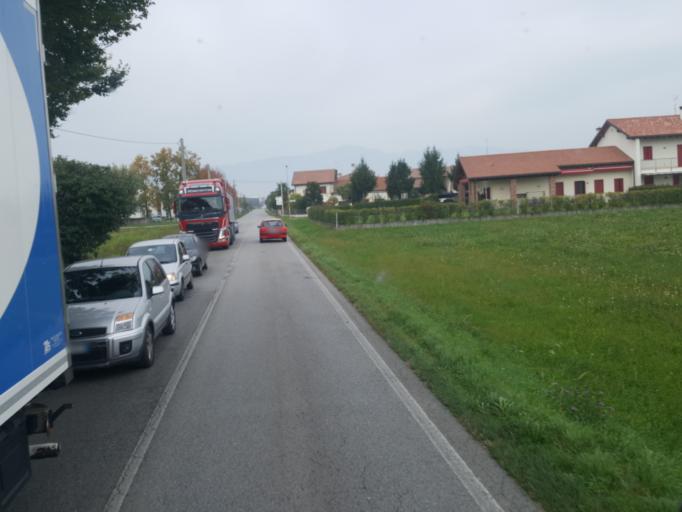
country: IT
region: Veneto
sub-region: Provincia di Treviso
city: Castello di Godego
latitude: 45.7017
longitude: 11.8739
